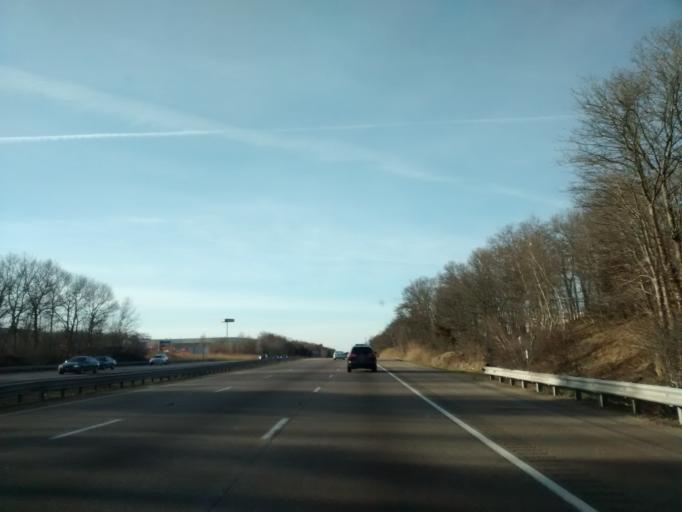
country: US
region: Massachusetts
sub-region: Norfolk County
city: Avon
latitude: 42.1328
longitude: -71.0637
